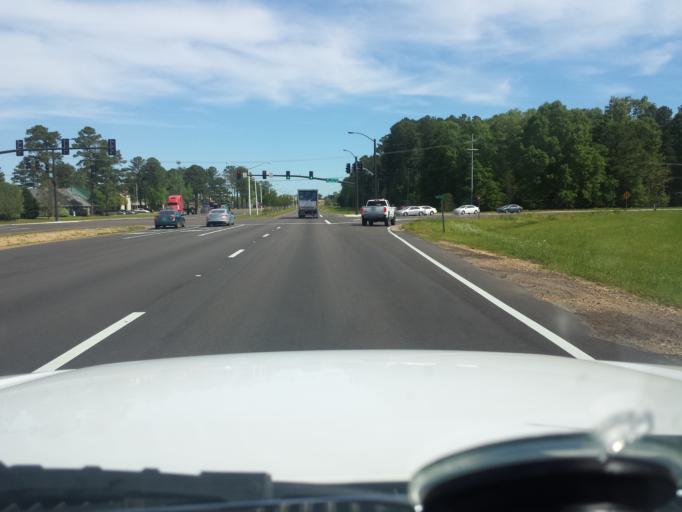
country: US
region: Mississippi
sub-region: Rankin County
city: Flowood
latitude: 32.3287
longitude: -90.0910
